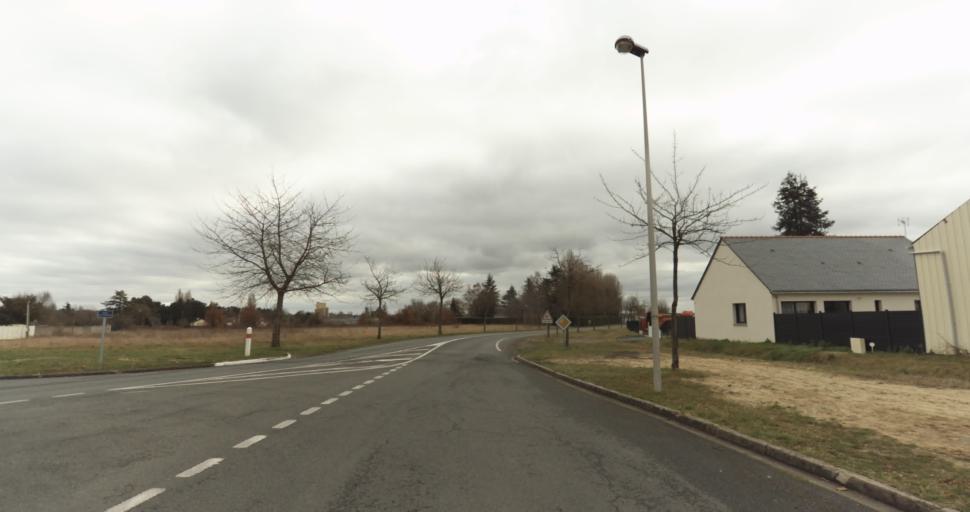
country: FR
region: Pays de la Loire
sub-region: Departement de Maine-et-Loire
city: Saint-Philbert-du-Peuple
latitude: 47.3776
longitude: -0.0988
